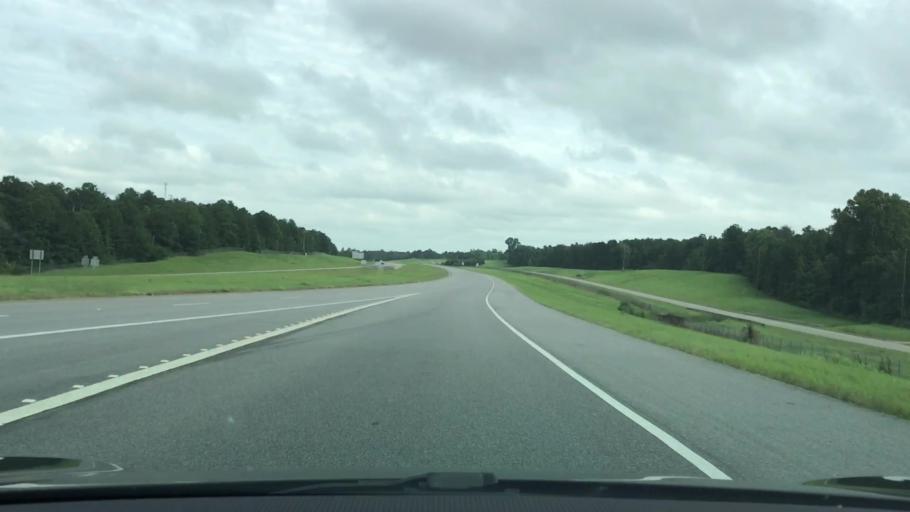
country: US
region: Alabama
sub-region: Montgomery County
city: Pike Road
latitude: 32.3409
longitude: -86.0634
